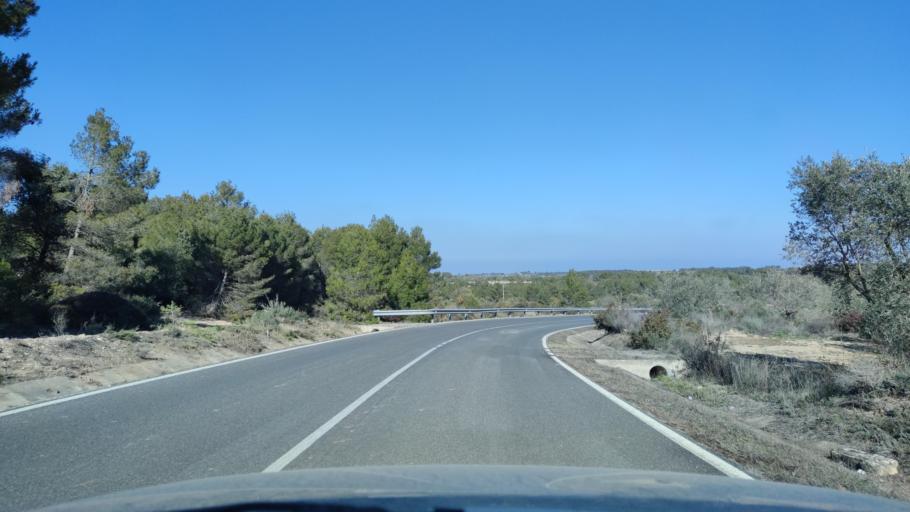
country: ES
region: Catalonia
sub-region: Provincia de Lleida
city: Maials
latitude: 41.3376
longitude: 0.4605
